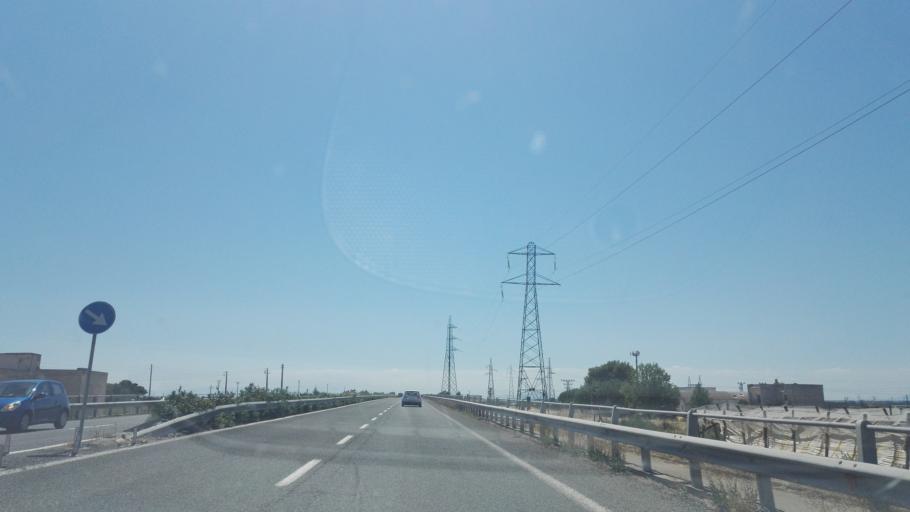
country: IT
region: Apulia
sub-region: Provincia di Taranto
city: Marina di Ginosa
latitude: 40.4454
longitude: 16.8532
